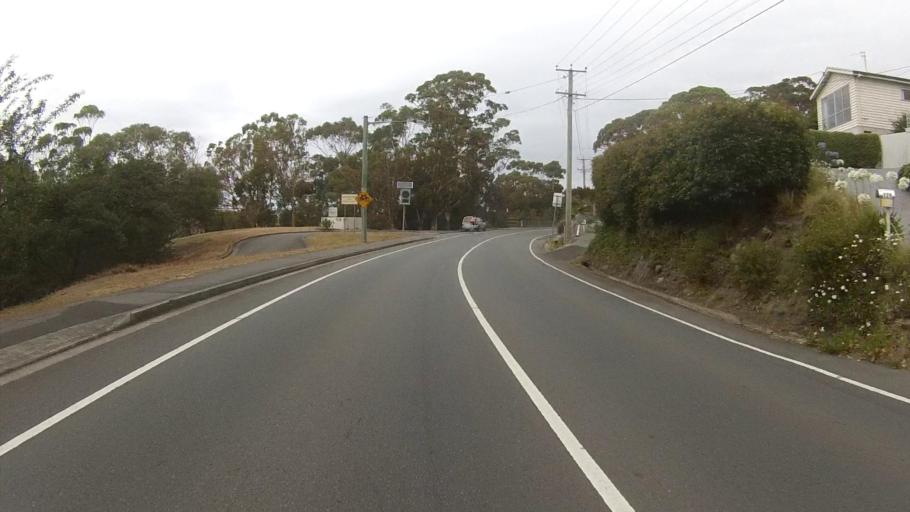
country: AU
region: Tasmania
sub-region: Kingborough
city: Taroona
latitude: -42.9414
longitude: 147.3526
